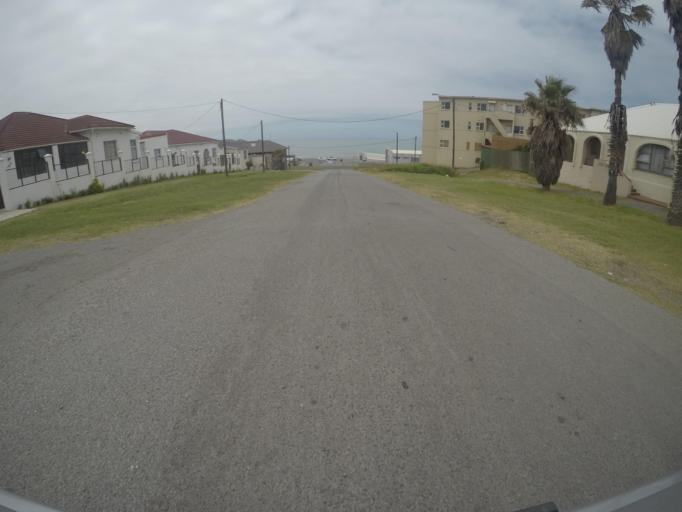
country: ZA
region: Eastern Cape
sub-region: Buffalo City Metropolitan Municipality
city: East London
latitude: -33.0146
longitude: 27.9189
